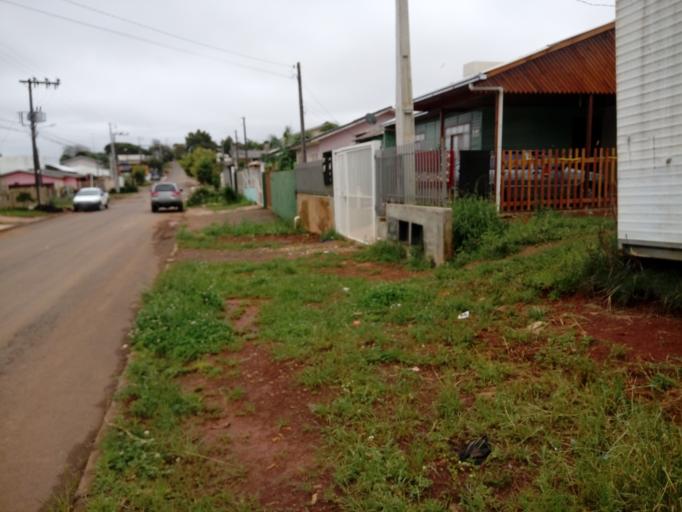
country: BR
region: Santa Catarina
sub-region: Chapeco
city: Chapeco
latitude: -27.1043
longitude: -52.5921
